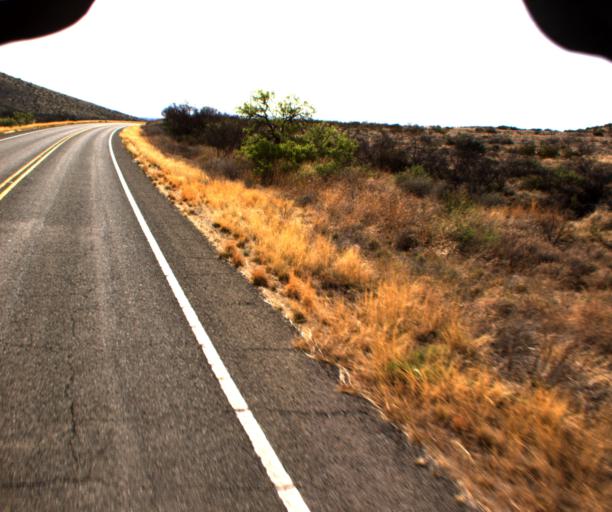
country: US
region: Arizona
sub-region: Cochise County
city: Willcox
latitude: 32.1824
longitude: -109.6554
